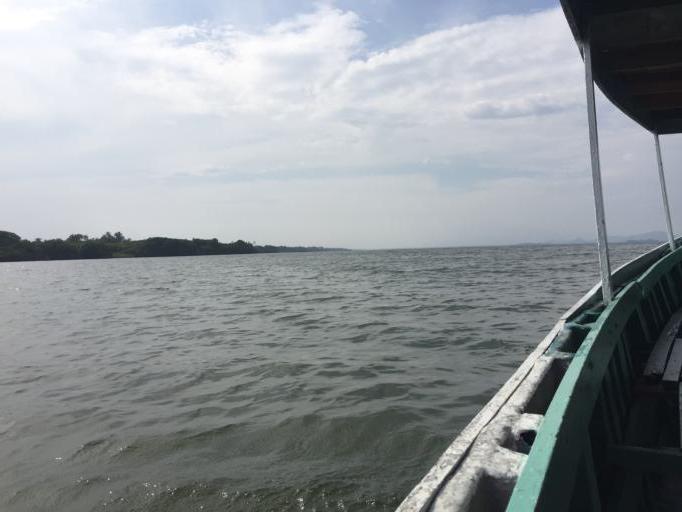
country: MX
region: Guerrero
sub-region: Coyuca de Benitez
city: Colonia Luces en el Mar
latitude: 16.9127
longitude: -99.9780
